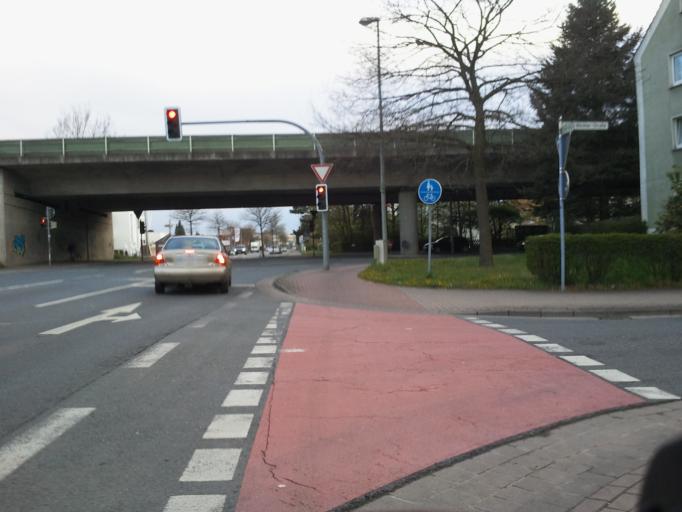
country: DE
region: Lower Saxony
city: Nienburg
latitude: 52.6542
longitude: 9.2228
